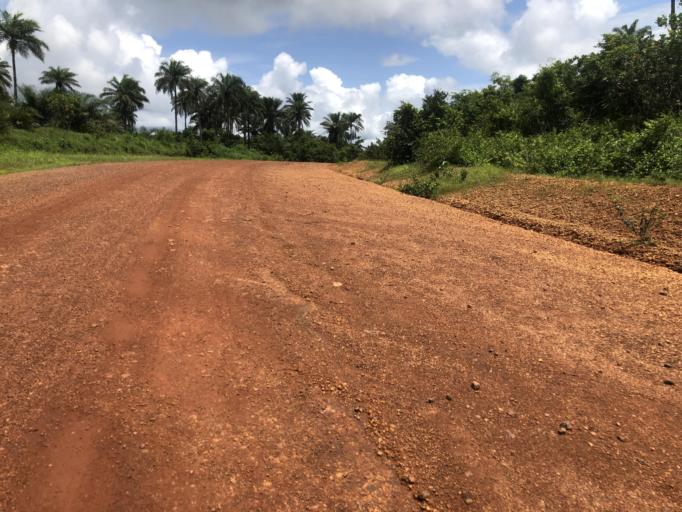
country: SL
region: Northern Province
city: Port Loko
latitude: 8.7133
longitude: -12.8298
